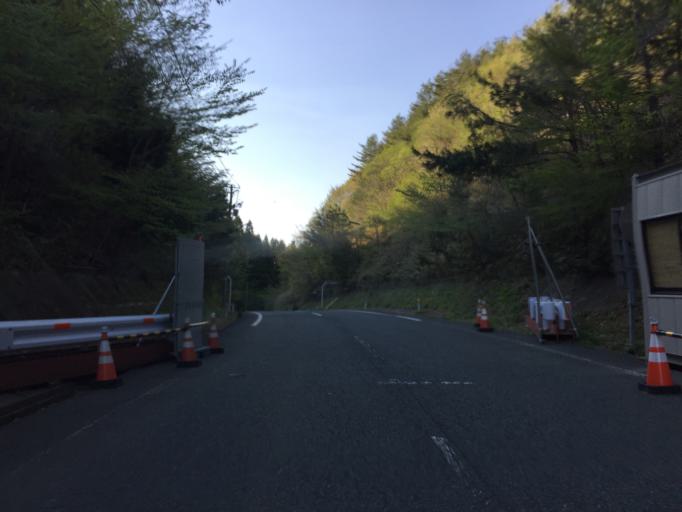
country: JP
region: Fukushima
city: Funehikimachi-funehiki
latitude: 37.5330
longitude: 140.7461
